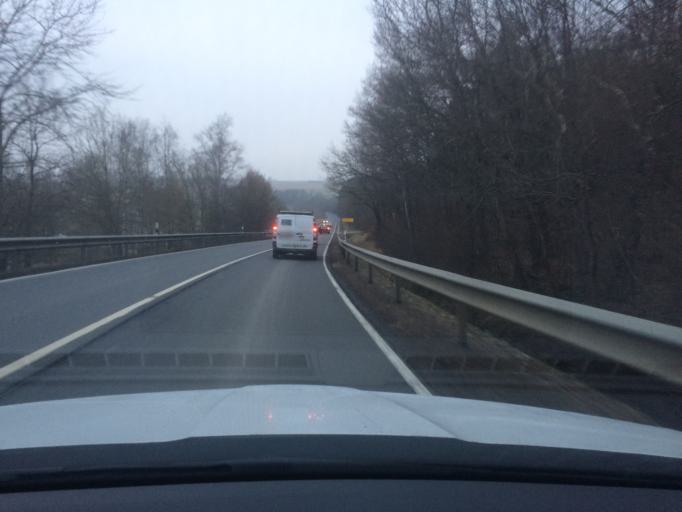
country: DE
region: Rheinland-Pfalz
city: Kludenbach
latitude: 49.9880
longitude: 7.3781
